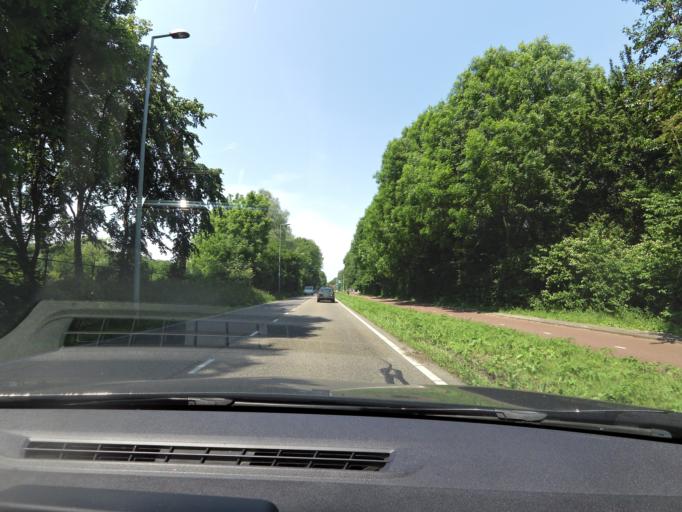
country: NL
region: South Holland
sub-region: Gemeente Rotterdam
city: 's-Gravenland
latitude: 51.9347
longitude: 4.5318
